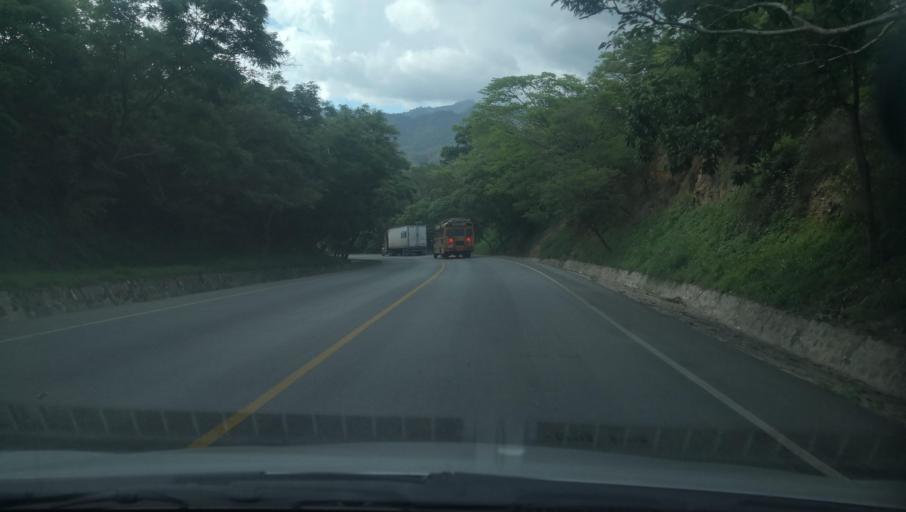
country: NI
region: Nueva Segovia
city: Ocotal
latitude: 13.6760
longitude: -86.4878
